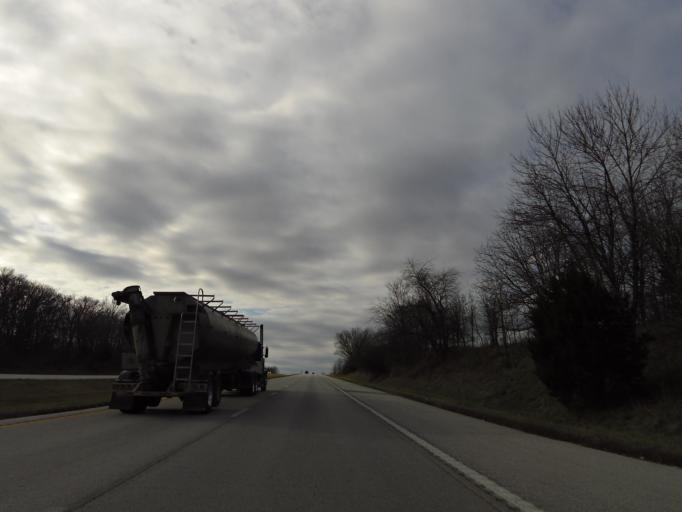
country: US
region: Missouri
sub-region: Marion County
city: Hannibal
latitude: 39.7441
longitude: -91.4331
